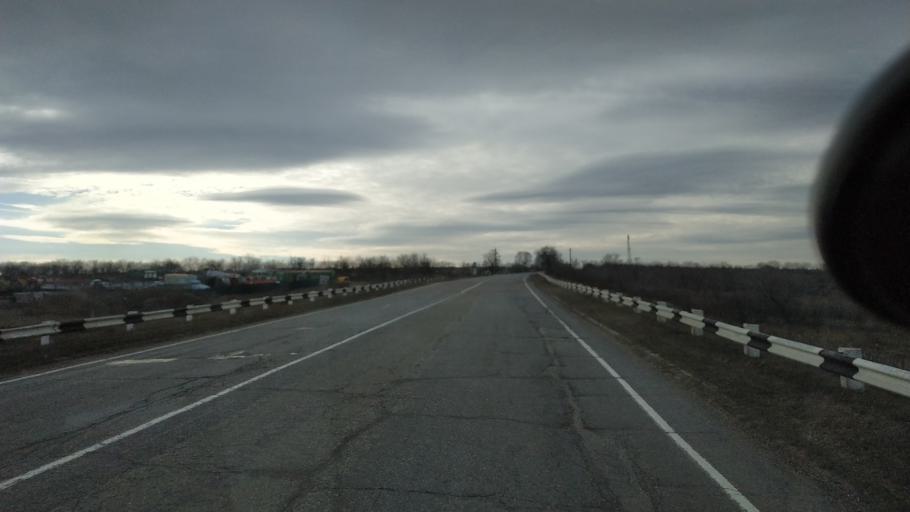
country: MD
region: Chisinau
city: Vadul lui Voda
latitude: 47.0893
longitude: 29.0627
